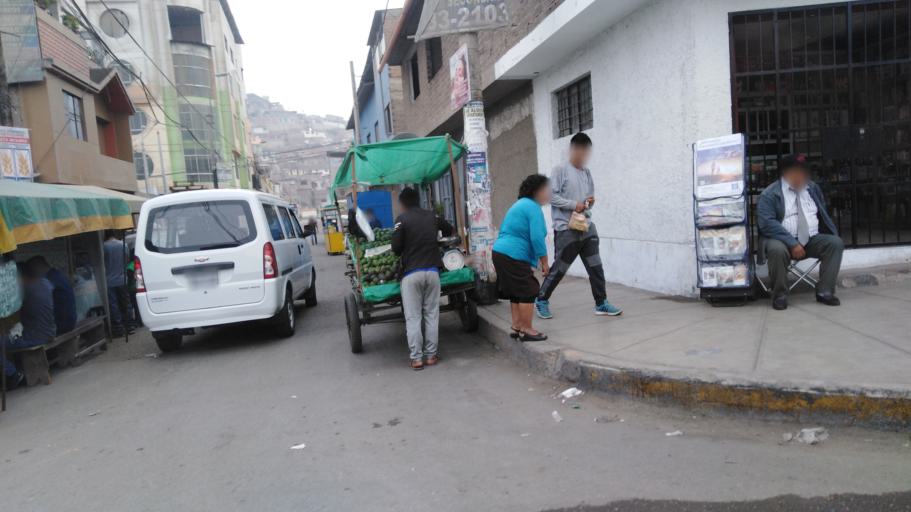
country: PE
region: Lima
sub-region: Lima
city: La Molina
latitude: -12.1431
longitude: -76.9444
